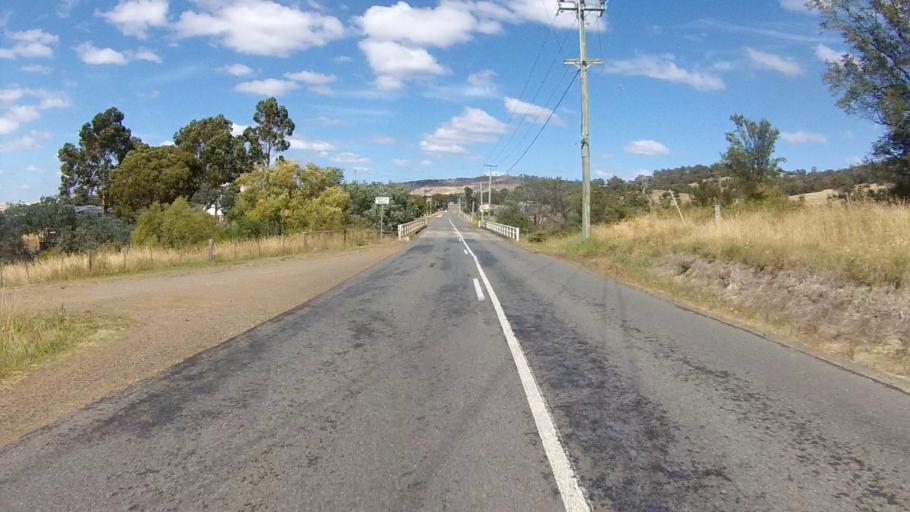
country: AU
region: Tasmania
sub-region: Clarence
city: Cambridge
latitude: -42.6579
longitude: 147.4259
